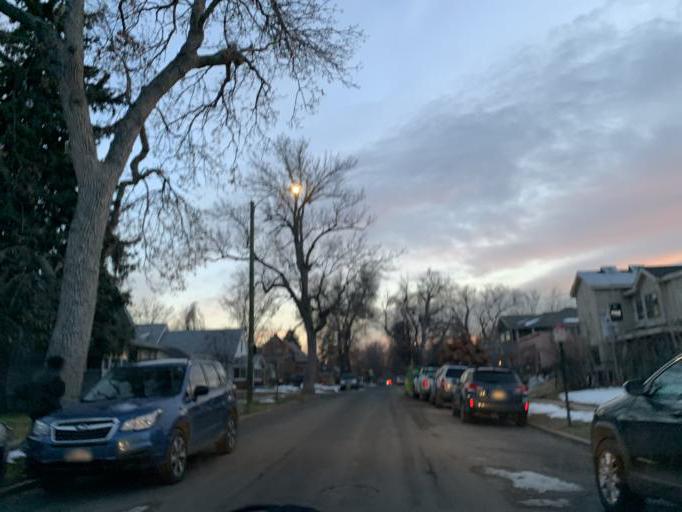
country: US
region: Colorado
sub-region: Adams County
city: Berkley
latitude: 39.7777
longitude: -105.0404
